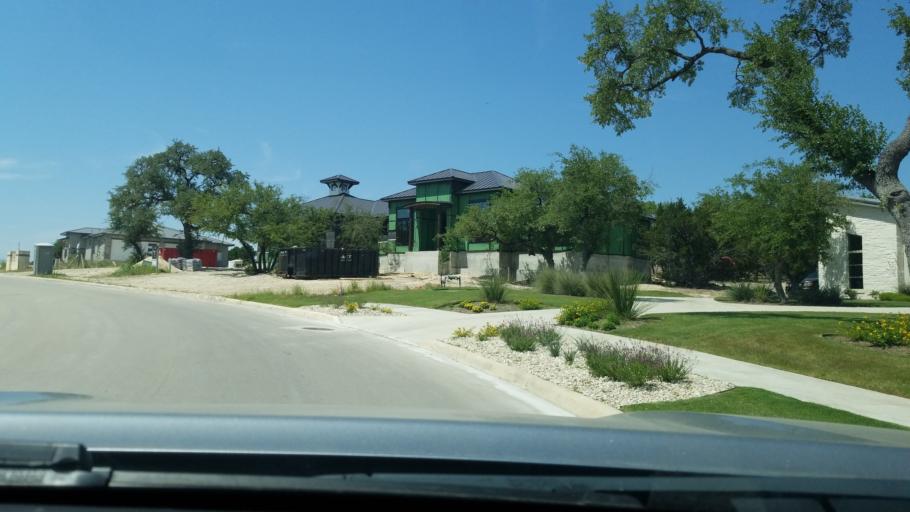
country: US
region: Texas
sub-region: Kendall County
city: Boerne
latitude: 29.7924
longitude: -98.6922
